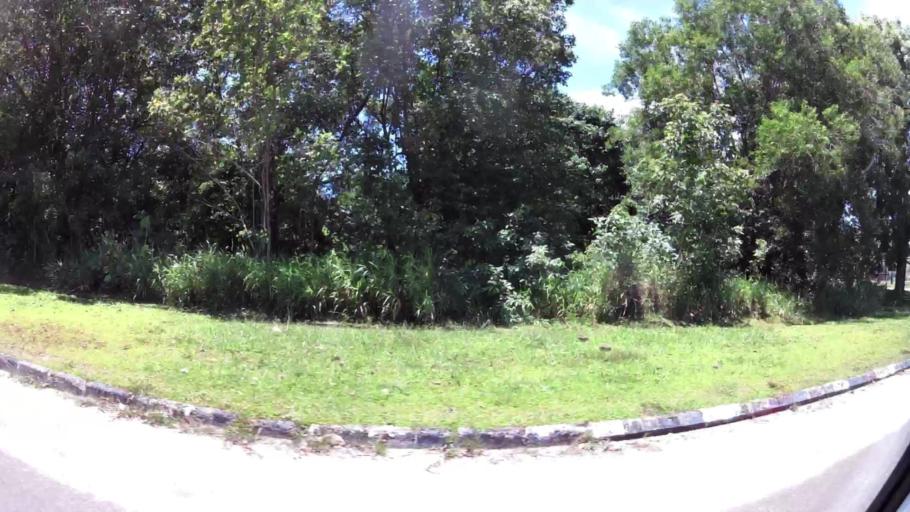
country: BN
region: Brunei and Muara
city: Bandar Seri Begawan
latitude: 4.9229
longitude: 114.9447
